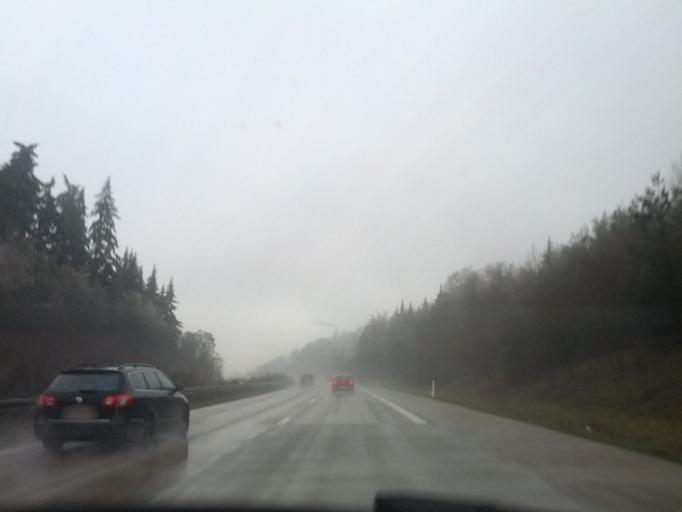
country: DE
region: Bavaria
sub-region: Regierungsbezirk Mittelfranken
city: Schillingsfurst
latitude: 49.2748
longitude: 10.2353
